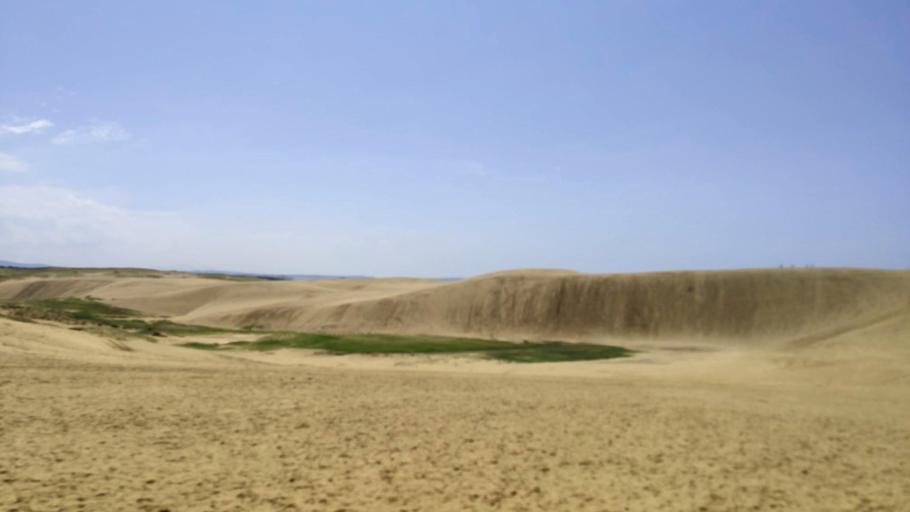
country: JP
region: Tottori
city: Tottori
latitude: 35.5435
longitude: 134.2351
